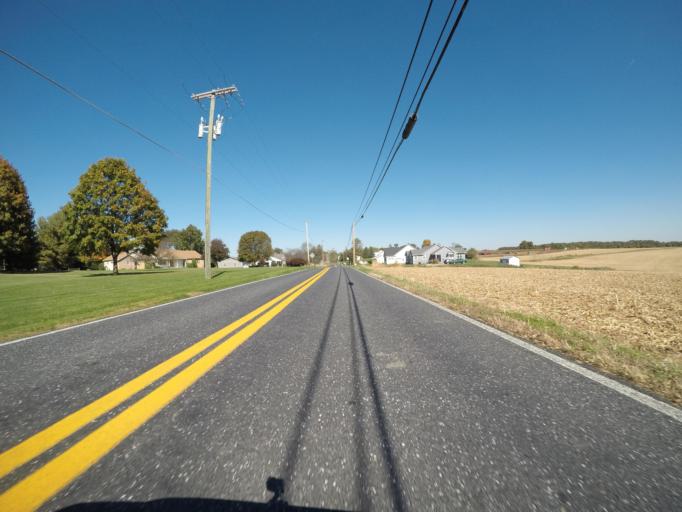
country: US
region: Maryland
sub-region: Carroll County
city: Hampstead
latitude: 39.5667
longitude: -76.8816
